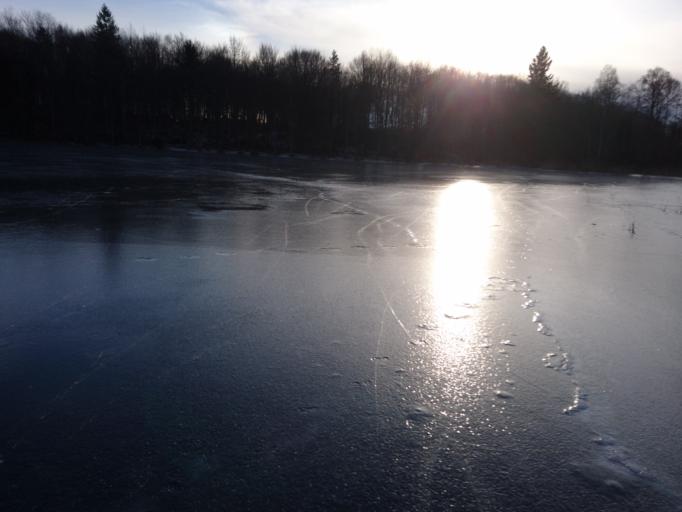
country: SE
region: Blekinge
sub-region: Karlshamns Kommun
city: Karlshamn
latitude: 56.2338
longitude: 14.9716
